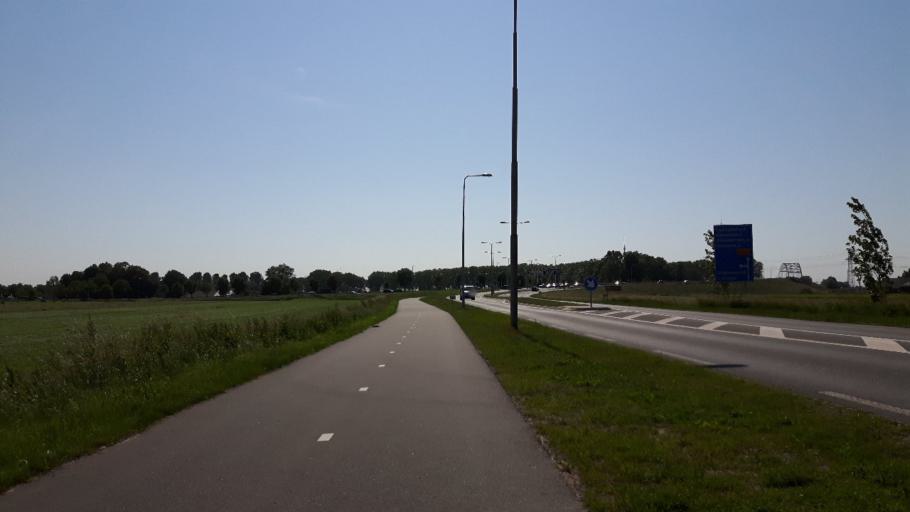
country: NL
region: Utrecht
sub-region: Stichtse Vecht
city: Vreeland
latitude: 52.2254
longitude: 5.0167
